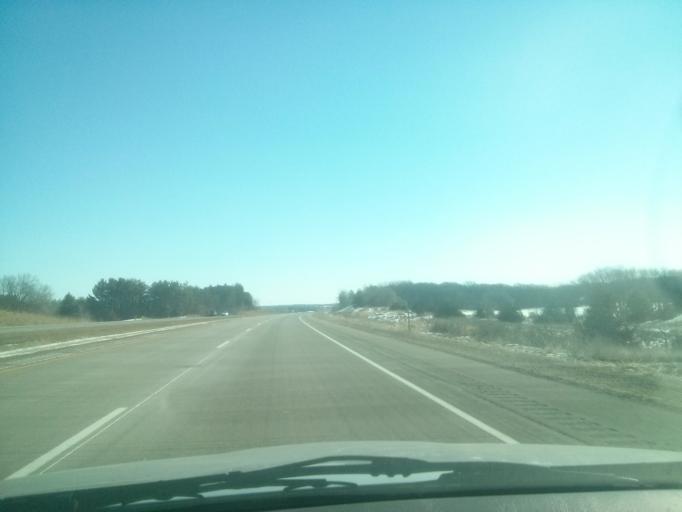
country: US
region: Wisconsin
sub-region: Saint Croix County
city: Somerset
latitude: 45.1078
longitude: -92.7093
